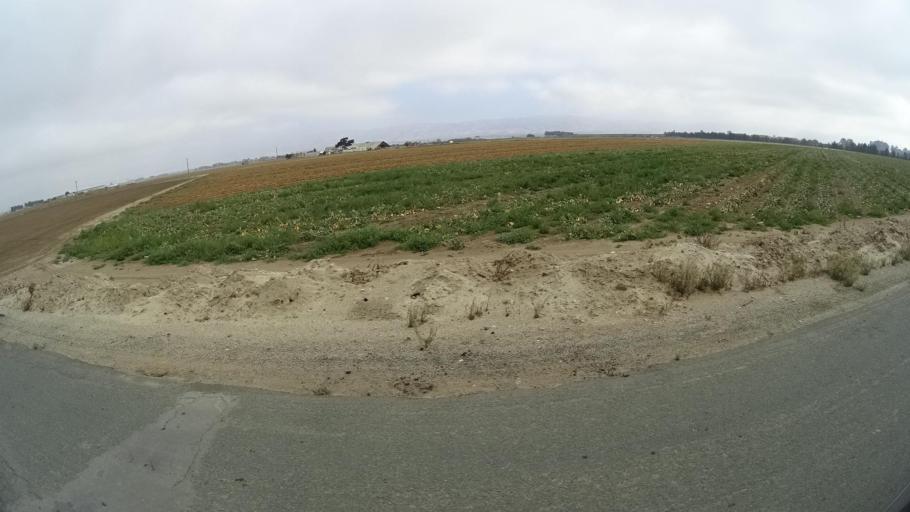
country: US
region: California
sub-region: Monterey County
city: Soledad
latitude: 36.3735
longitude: -121.3234
